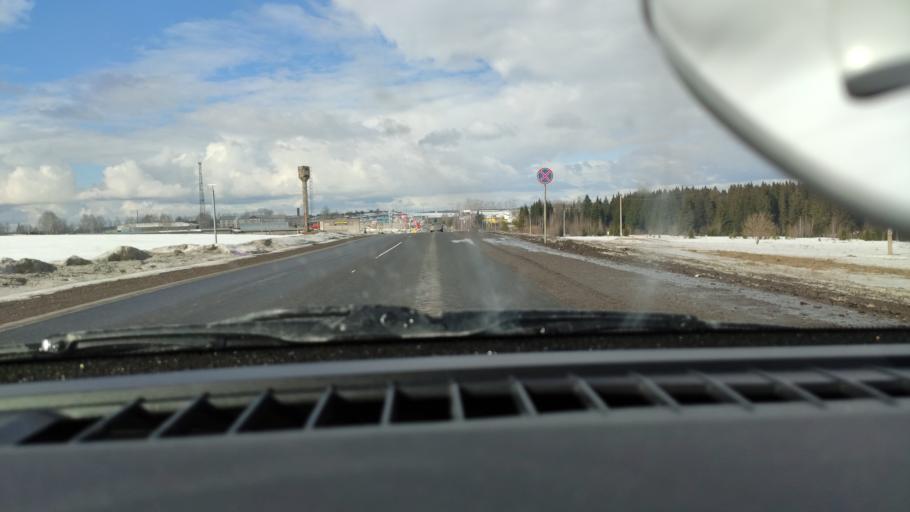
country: RU
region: Perm
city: Nytva
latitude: 57.9454
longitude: 55.3638
